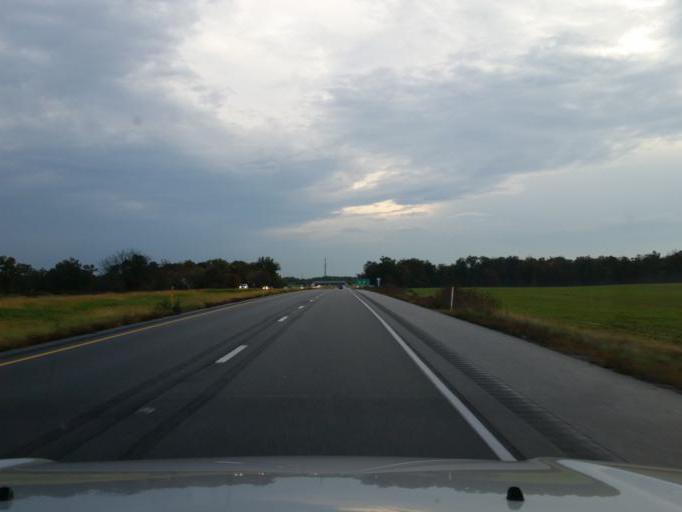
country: US
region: Pennsylvania
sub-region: Adams County
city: Biglerville
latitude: 39.8967
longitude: -77.1758
